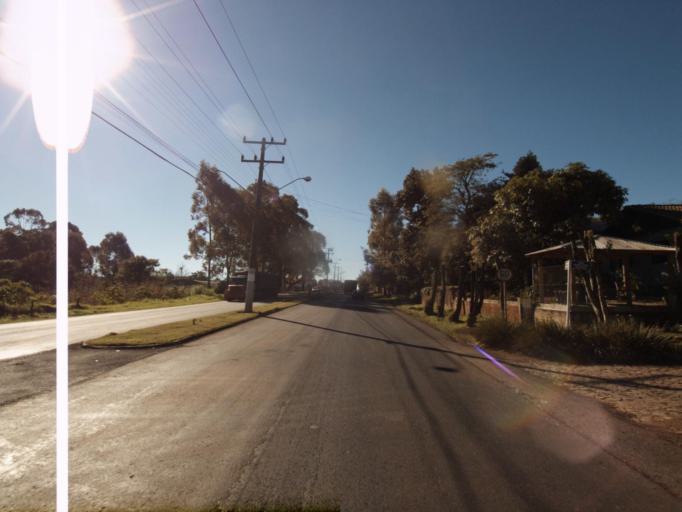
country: AR
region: Misiones
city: Bernardo de Irigoyen
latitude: -26.7505
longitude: -53.5008
